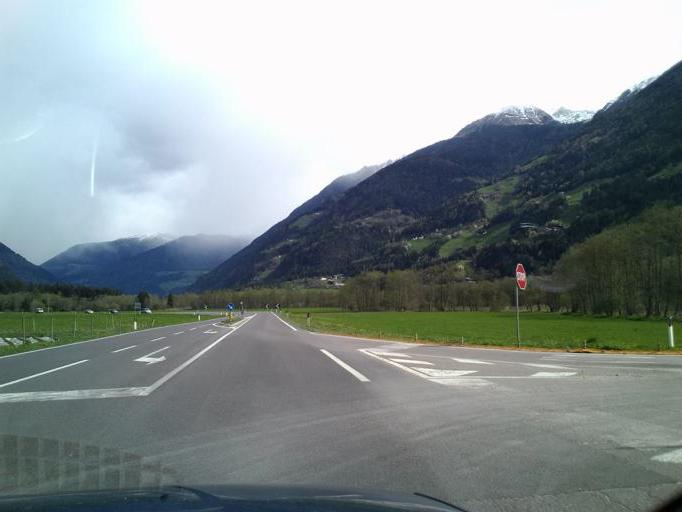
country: IT
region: Trentino-Alto Adige
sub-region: Bolzano
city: Gais
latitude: 46.8471
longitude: 11.9495
